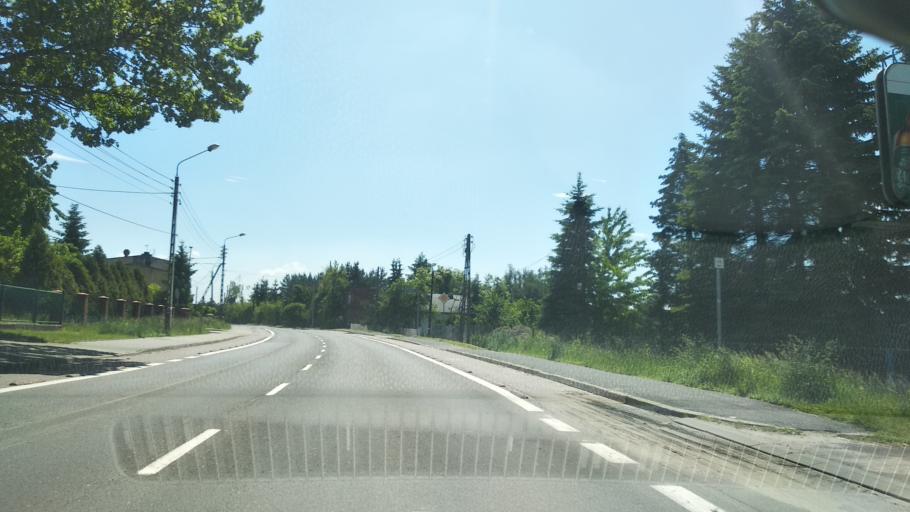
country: PL
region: Silesian Voivodeship
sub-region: Ruda Slaska
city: Ruda Slaska
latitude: 50.2464
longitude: 18.9033
